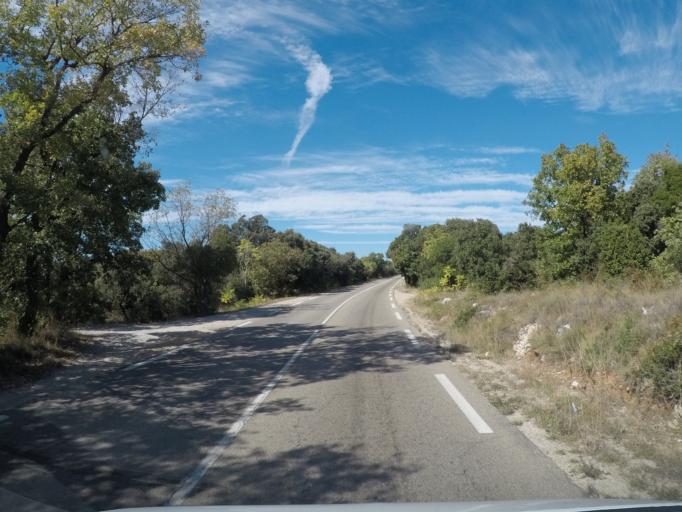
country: FR
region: Languedoc-Roussillon
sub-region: Departement de l'Herault
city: Saint-Martin-de-Londres
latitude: 43.7612
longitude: 3.7481
